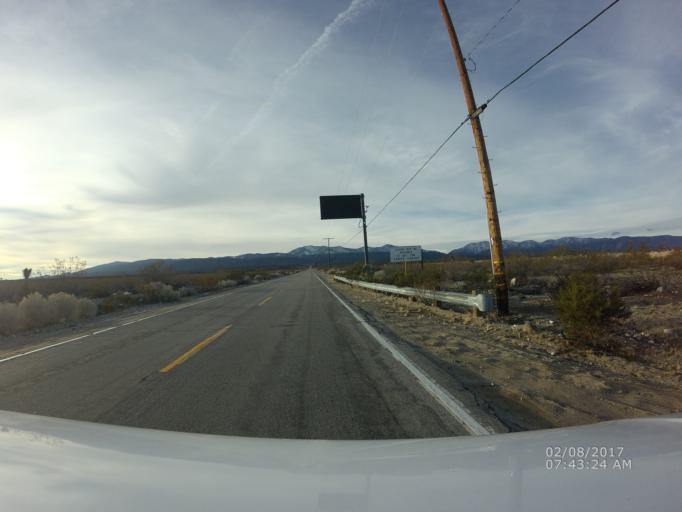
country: US
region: California
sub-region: Los Angeles County
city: Lake Los Angeles
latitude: 34.4975
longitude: -117.7652
